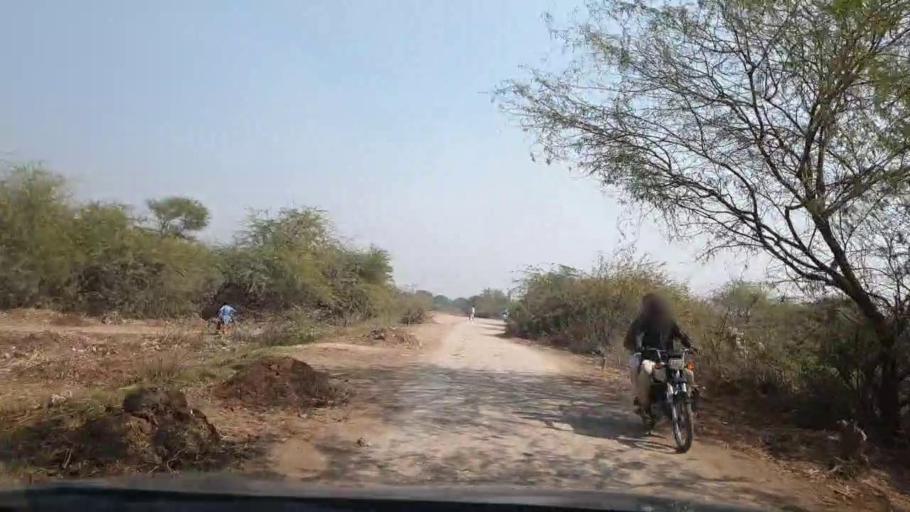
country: PK
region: Sindh
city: Tando Allahyar
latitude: 25.5006
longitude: 68.7952
